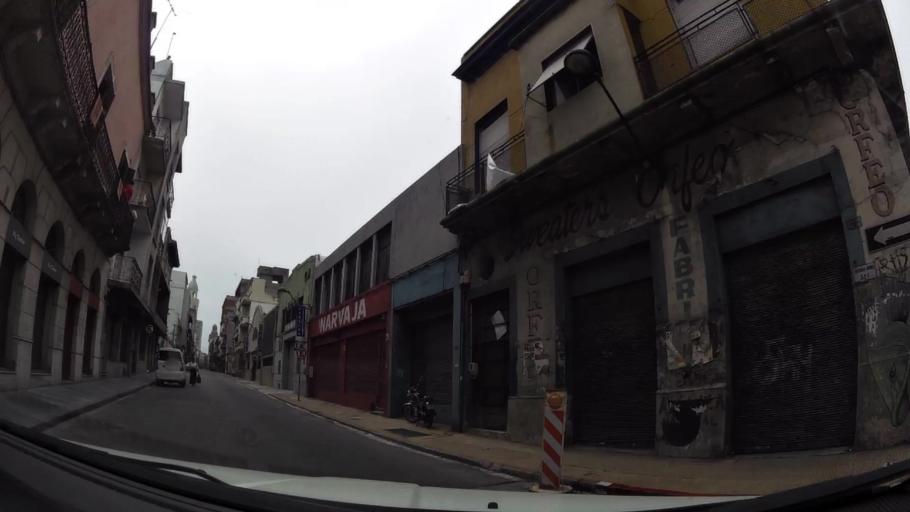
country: UY
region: Montevideo
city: Montevideo
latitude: -34.9096
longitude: -56.2084
